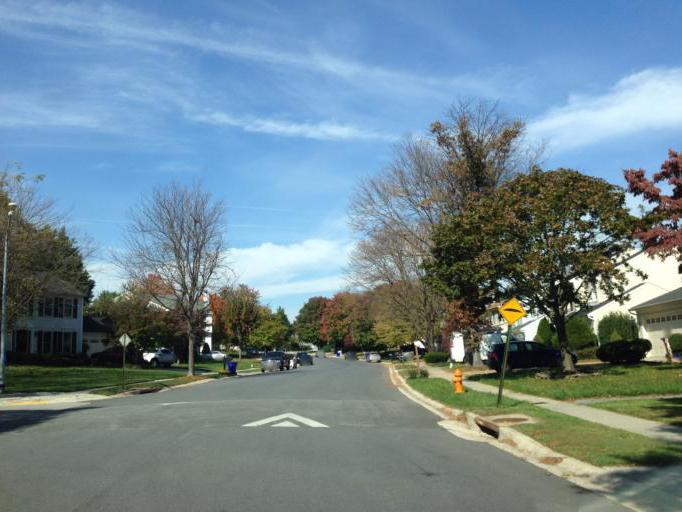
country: US
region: Maryland
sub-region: Howard County
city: Ellicott City
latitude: 39.2471
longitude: -76.8136
